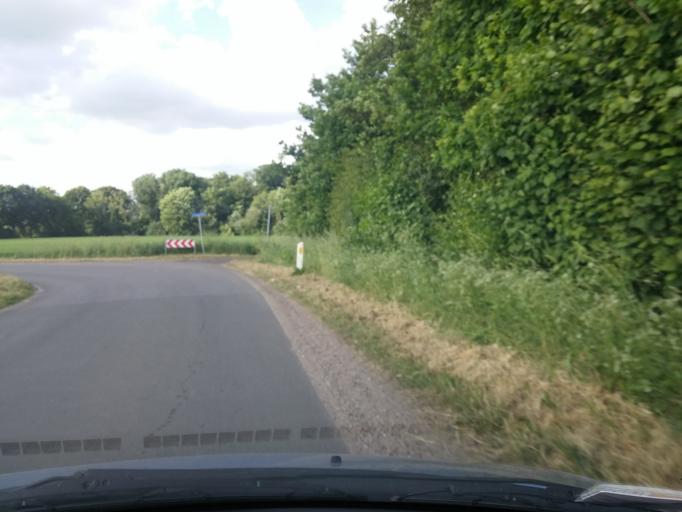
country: DK
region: South Denmark
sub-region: Kerteminde Kommune
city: Langeskov
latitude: 55.3894
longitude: 10.5727
